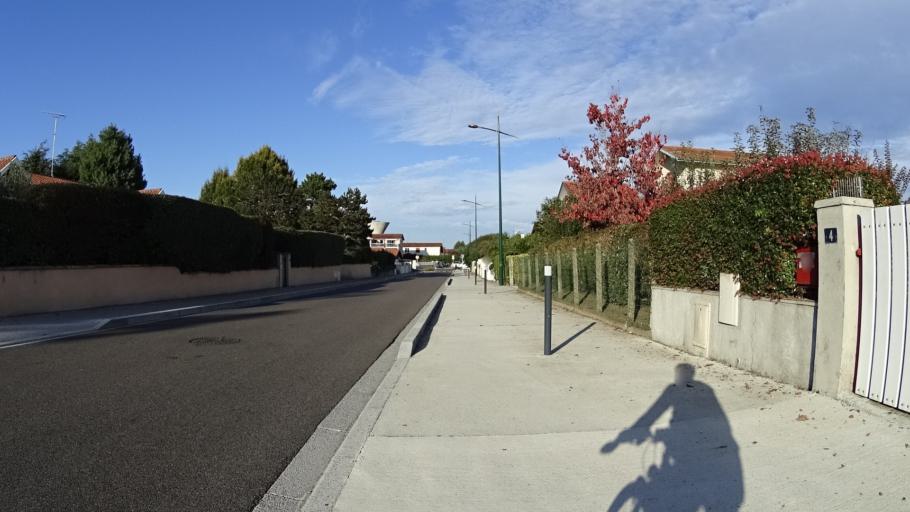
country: FR
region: Aquitaine
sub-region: Departement des Landes
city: Saint-Paul-les-Dax
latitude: 43.7280
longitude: -1.0600
